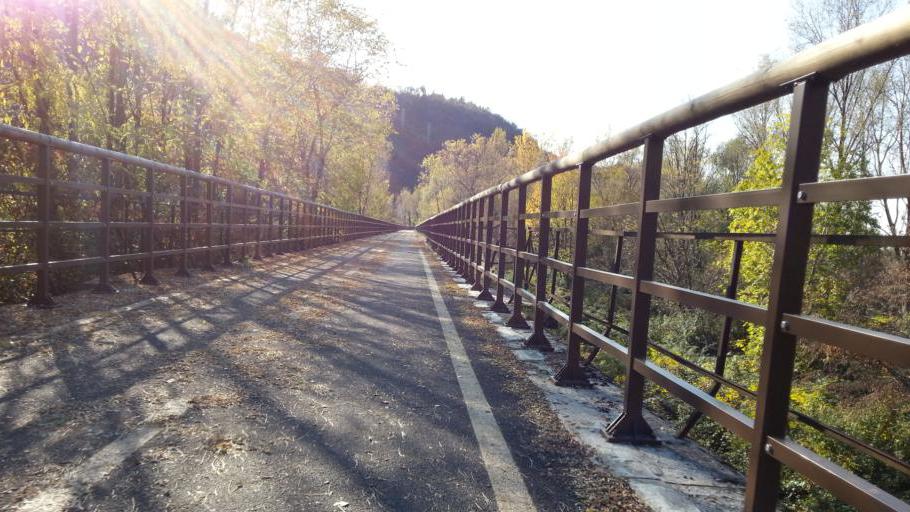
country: IT
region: Friuli Venezia Giulia
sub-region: Provincia di Udine
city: Venzone
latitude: 46.3121
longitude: 13.1274
